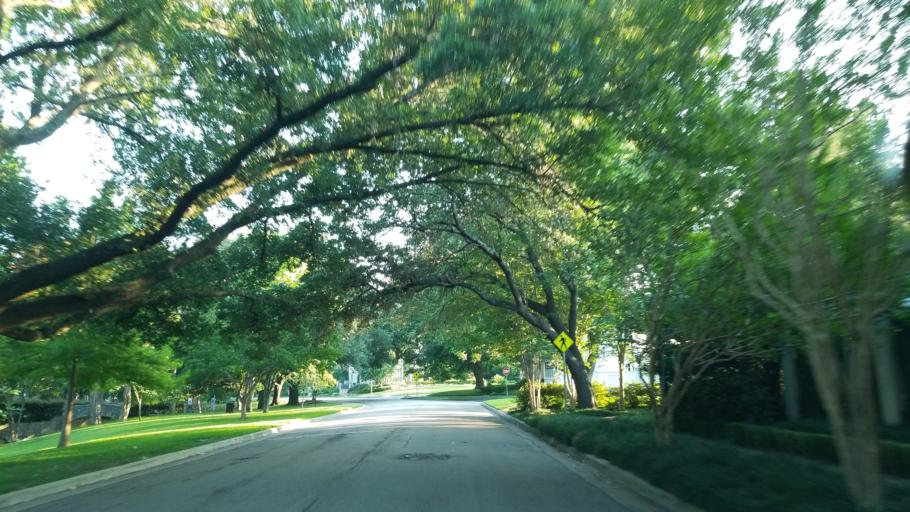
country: US
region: Texas
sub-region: Dallas County
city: Highland Park
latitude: 32.8346
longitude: -96.7923
